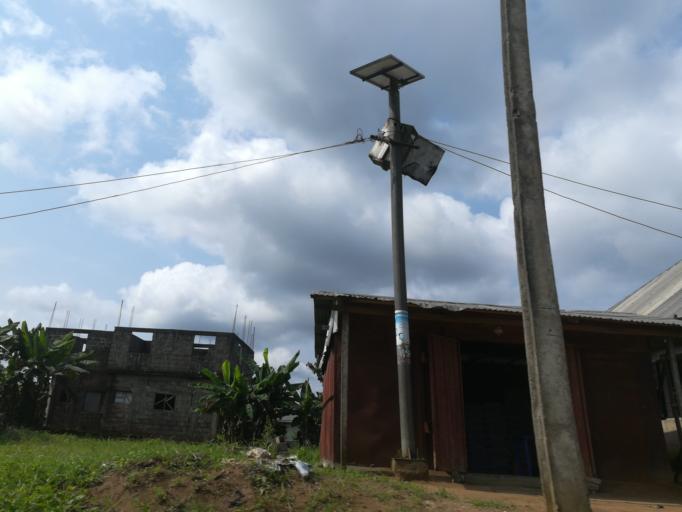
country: NG
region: Rivers
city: Okrika
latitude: 4.7427
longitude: 7.1154
